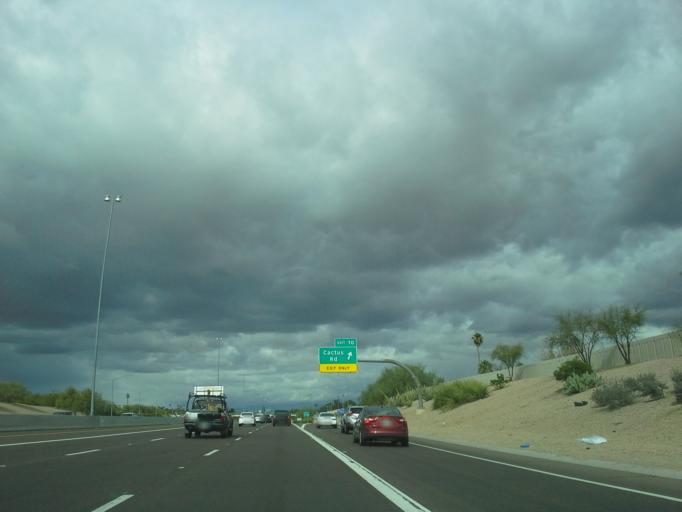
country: US
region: Arizona
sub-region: Maricopa County
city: Paradise Valley
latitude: 33.5917
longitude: -112.0093
